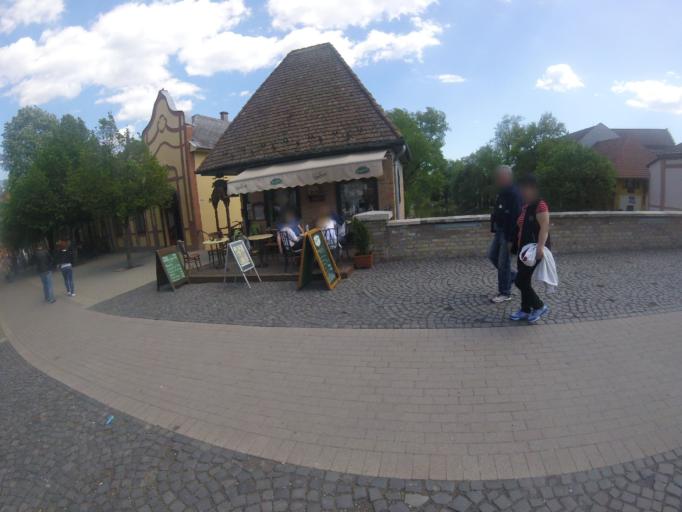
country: HU
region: Bekes
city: Gyula
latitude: 46.6446
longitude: 21.2732
